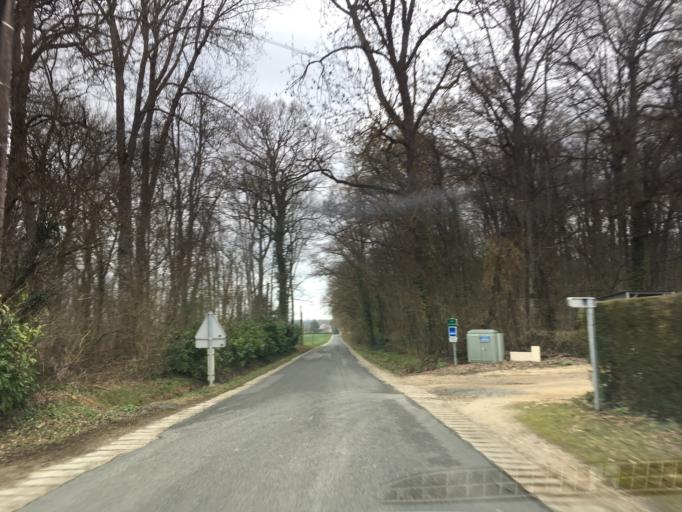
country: FR
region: Centre
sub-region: Departement d'Indre-et-Loire
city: Chanceaux-sur-Choisille
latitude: 47.4713
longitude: 0.7314
